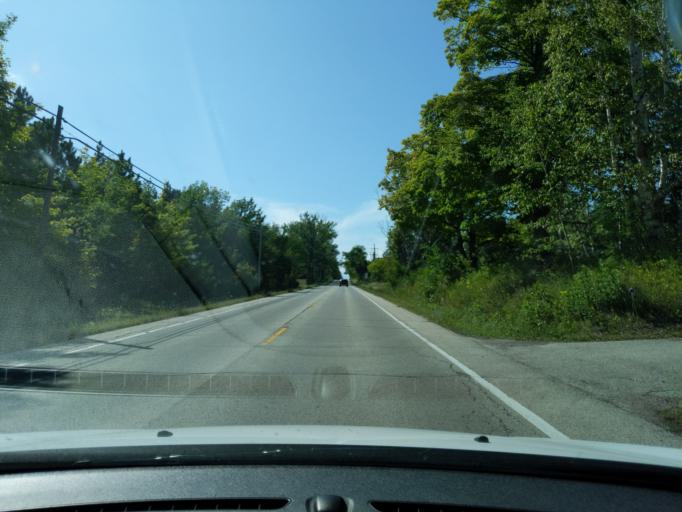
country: US
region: Michigan
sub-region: Delta County
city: Escanaba
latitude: 45.2595
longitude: -87.0280
